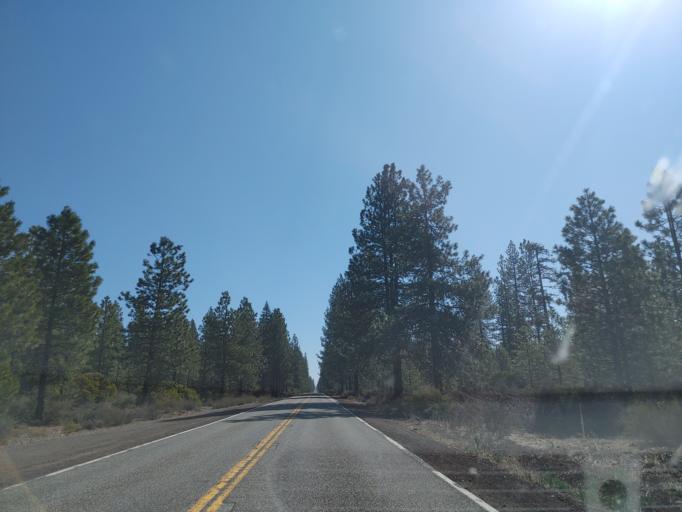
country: US
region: California
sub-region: Siskiyou County
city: McCloud
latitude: 41.2550
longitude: -122.0604
